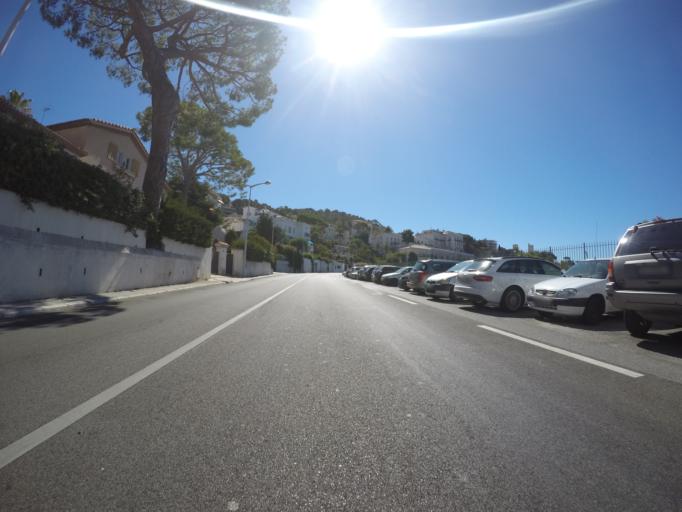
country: FR
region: Provence-Alpes-Cote d'Azur
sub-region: Departement des Alpes-Maritimes
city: Villefranche-sur-Mer
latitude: 43.6923
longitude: 7.2937
